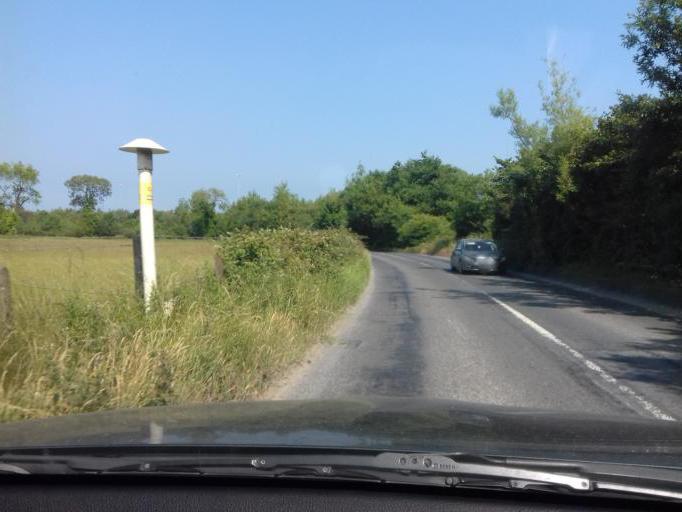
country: IE
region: Leinster
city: Balrothery
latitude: 53.5971
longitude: -6.2264
